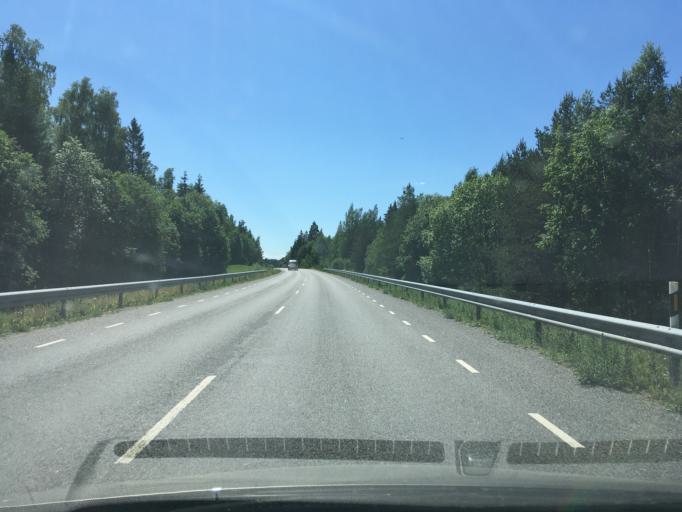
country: EE
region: Raplamaa
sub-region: Rapla vald
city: Rapla
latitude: 59.0066
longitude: 24.7692
